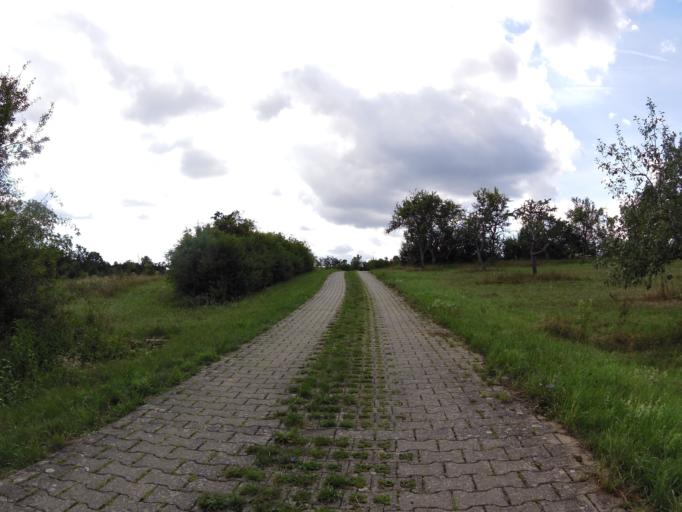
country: DE
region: Bavaria
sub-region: Regierungsbezirk Unterfranken
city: Margetshochheim
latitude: 49.8393
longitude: 9.8513
